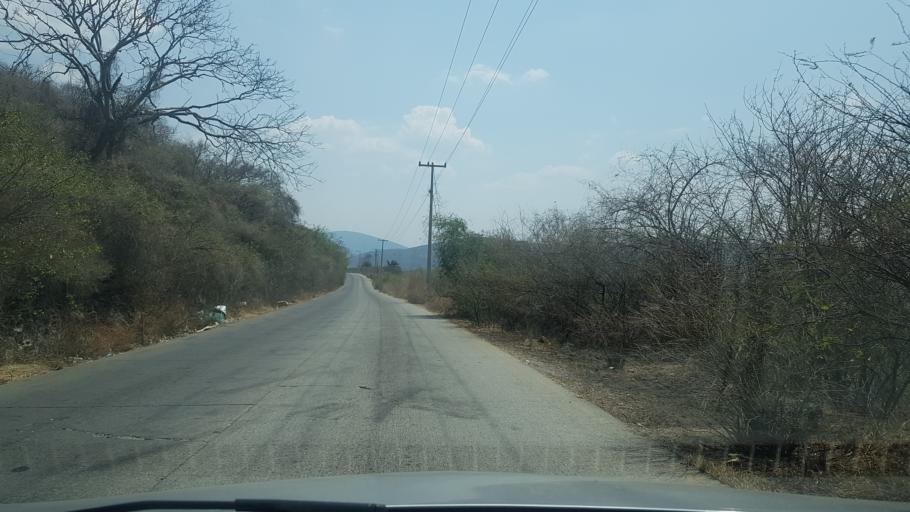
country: MX
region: Morelos
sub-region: Tlaltizapan de Zapata
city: Colonia Palo Prieto (Chipitongo)
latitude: 18.7419
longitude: -99.1139
